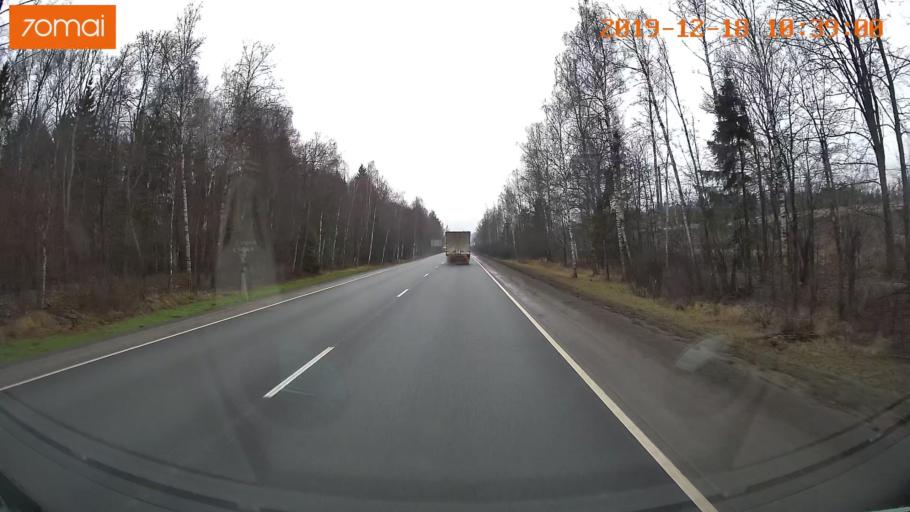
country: RU
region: Moskovskaya
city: Aprelevka
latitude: 55.4400
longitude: 37.1475
